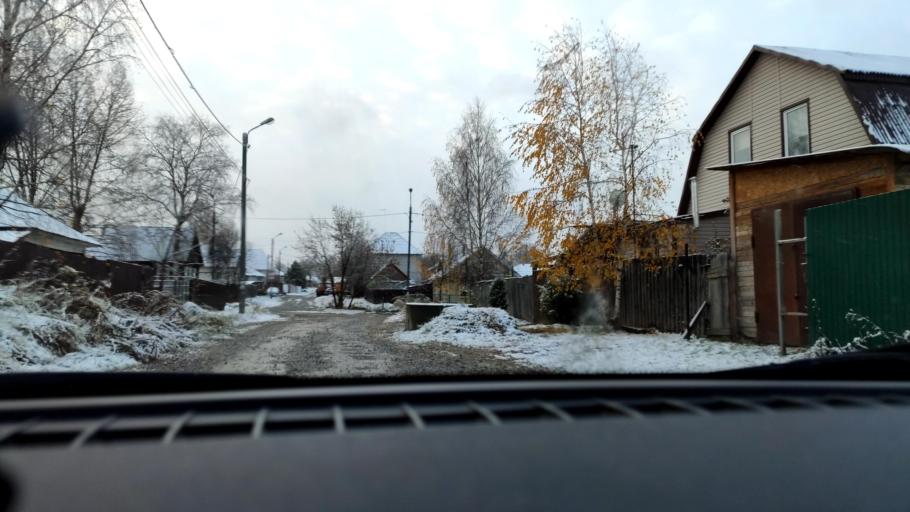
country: RU
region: Perm
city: Kondratovo
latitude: 58.0471
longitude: 56.0429
